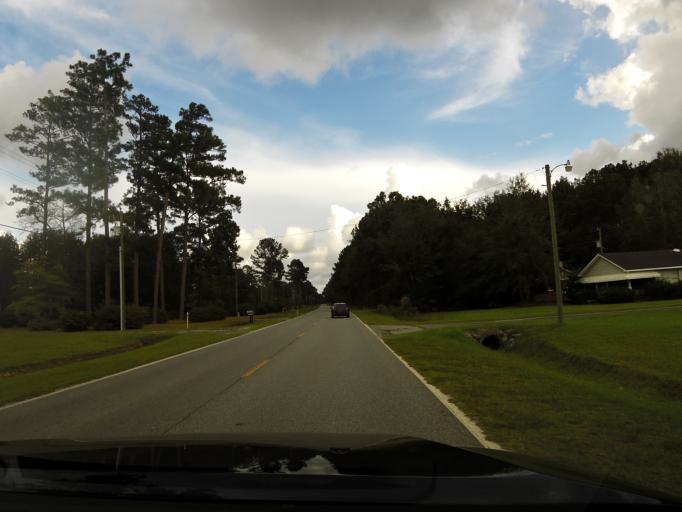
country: US
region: Georgia
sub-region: Liberty County
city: Midway
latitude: 31.8526
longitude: -81.4235
